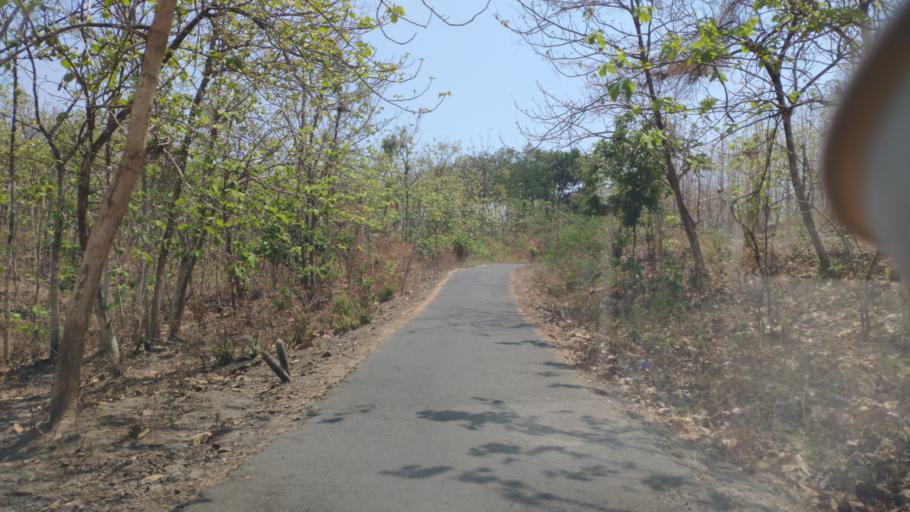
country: ID
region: Central Java
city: Menden
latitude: -7.3205
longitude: 111.4272
